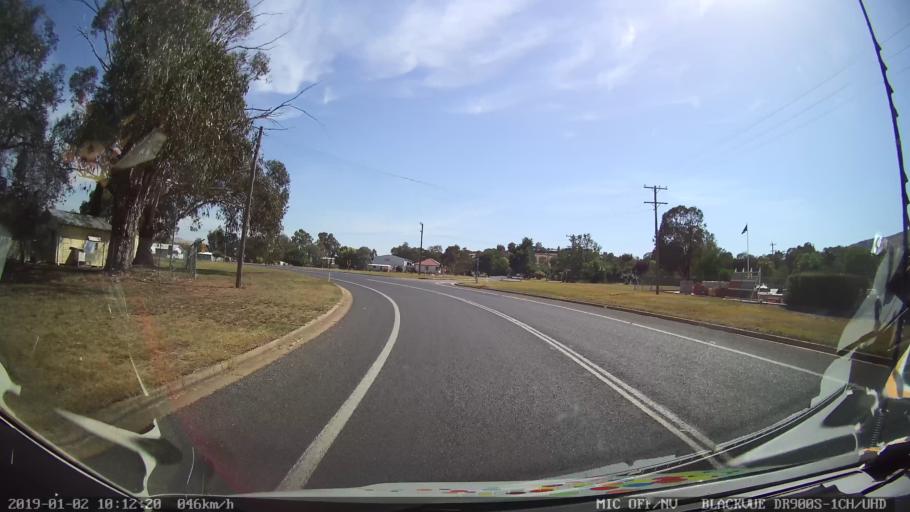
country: AU
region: New South Wales
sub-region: Gundagai
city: Gundagai
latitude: -35.0854
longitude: 148.0950
